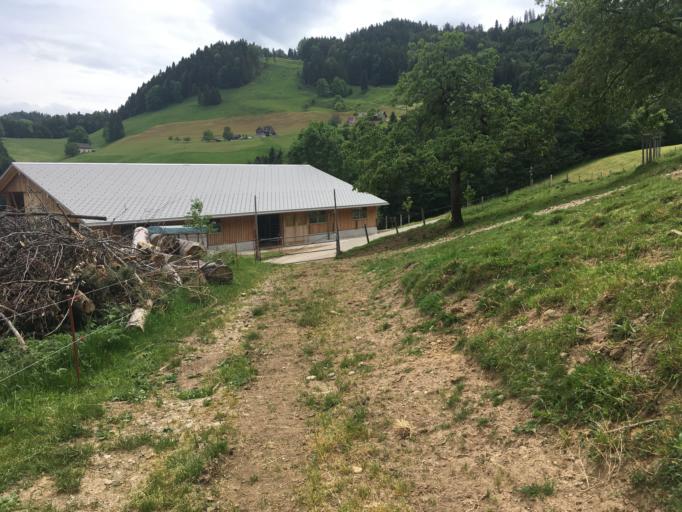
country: CH
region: Saint Gallen
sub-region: Wahlkreis Toggenburg
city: Lichtensteig
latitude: 47.3184
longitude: 9.0455
